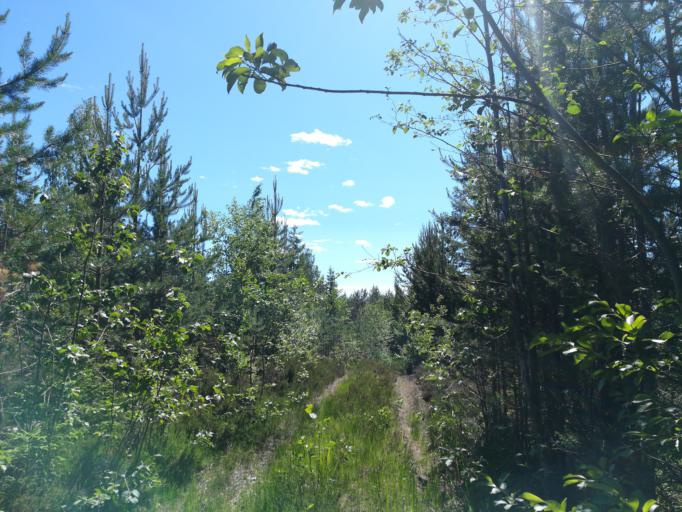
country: FI
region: Southern Savonia
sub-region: Mikkeli
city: Puumala
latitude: 61.6194
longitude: 28.1616
